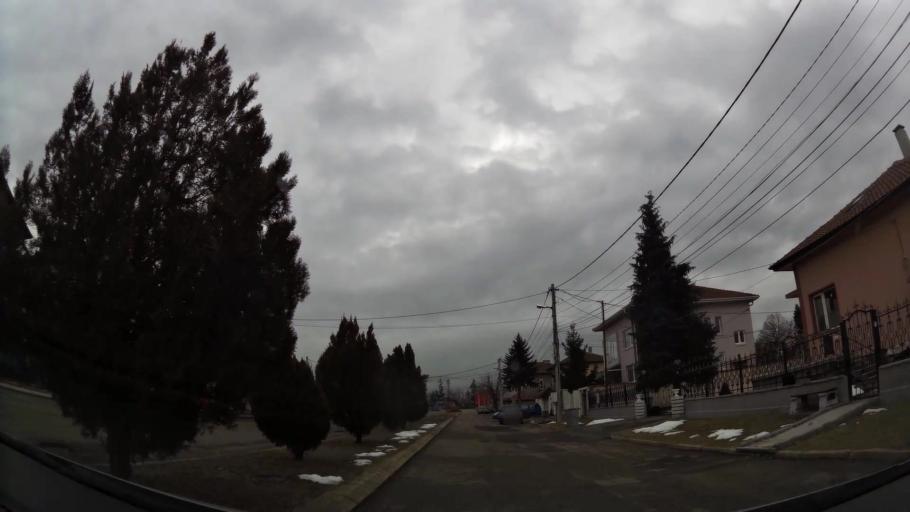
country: BG
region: Sofiya
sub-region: Obshtina Bozhurishte
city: Bozhurishte
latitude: 42.7397
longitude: 23.2662
